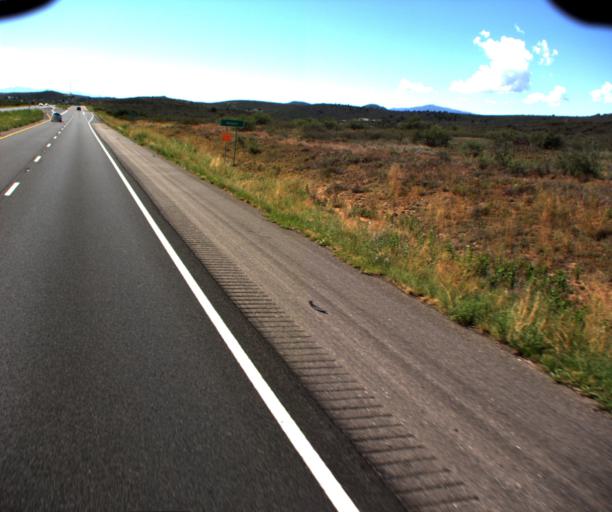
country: US
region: Arizona
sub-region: Yavapai County
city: Mayer
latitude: 34.4146
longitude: -112.2467
